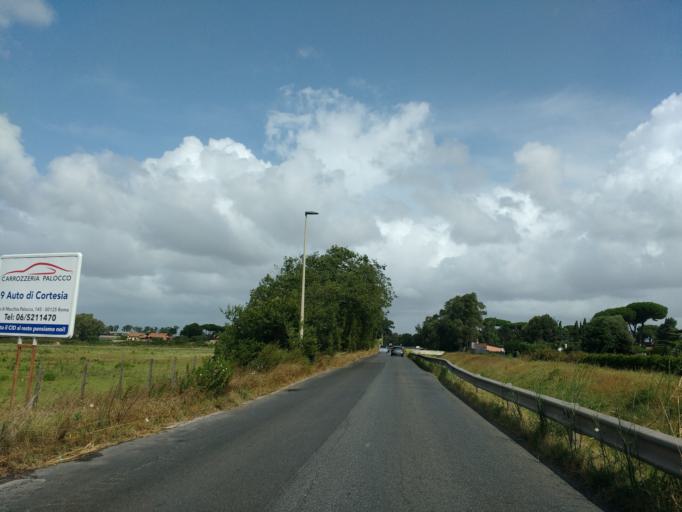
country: IT
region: Latium
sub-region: Citta metropolitana di Roma Capitale
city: Acilia-Castel Fusano-Ostia Antica
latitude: 41.7642
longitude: 12.3270
